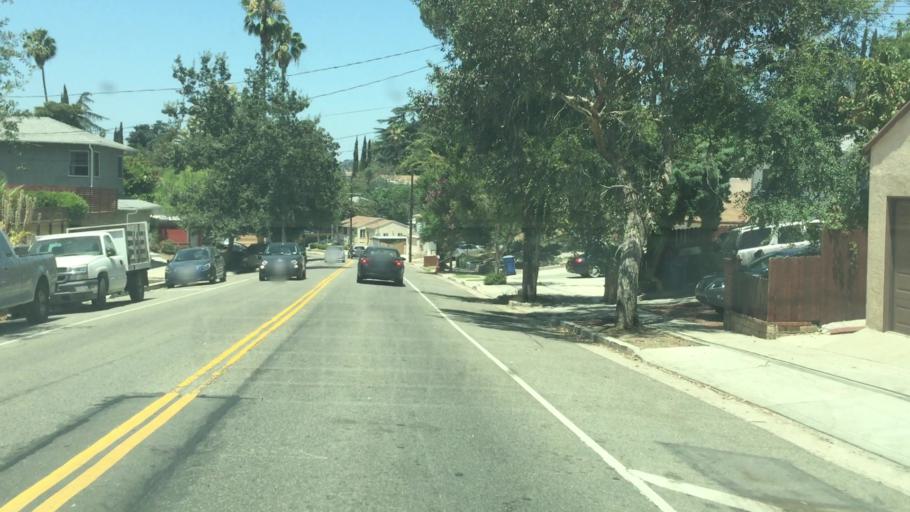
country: US
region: California
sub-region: Los Angeles County
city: Glendale
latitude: 34.1170
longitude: -118.2157
